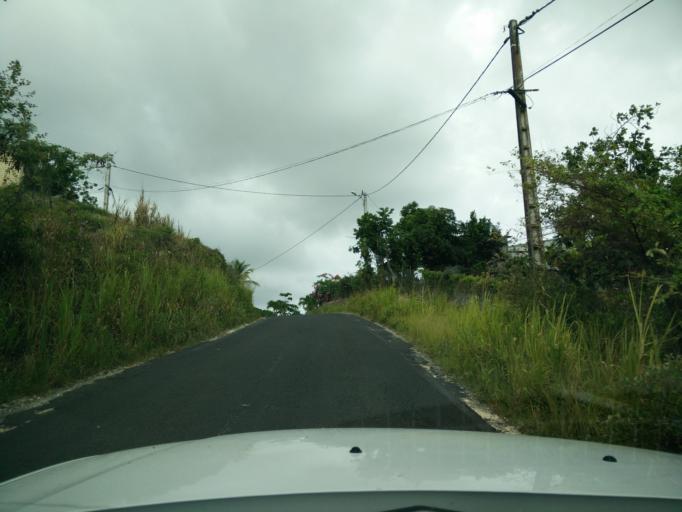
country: GP
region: Guadeloupe
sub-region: Guadeloupe
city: Le Gosier
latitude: 16.2397
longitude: -61.4470
